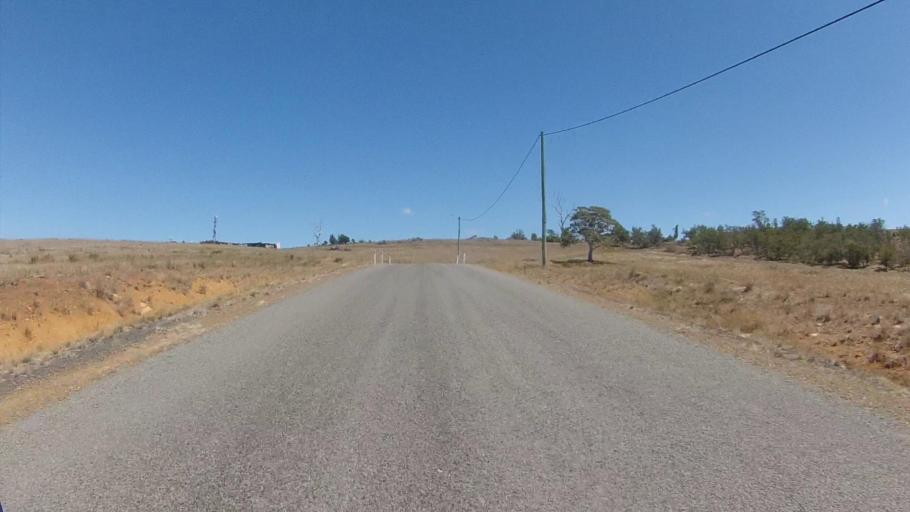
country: AU
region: Tasmania
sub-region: Sorell
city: Sorell
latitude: -42.7586
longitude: 147.5583
